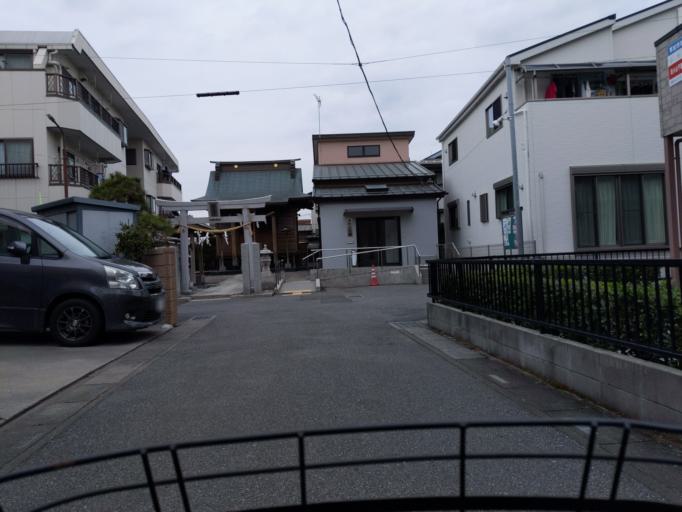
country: JP
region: Saitama
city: Soka
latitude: 35.8506
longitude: 139.7967
